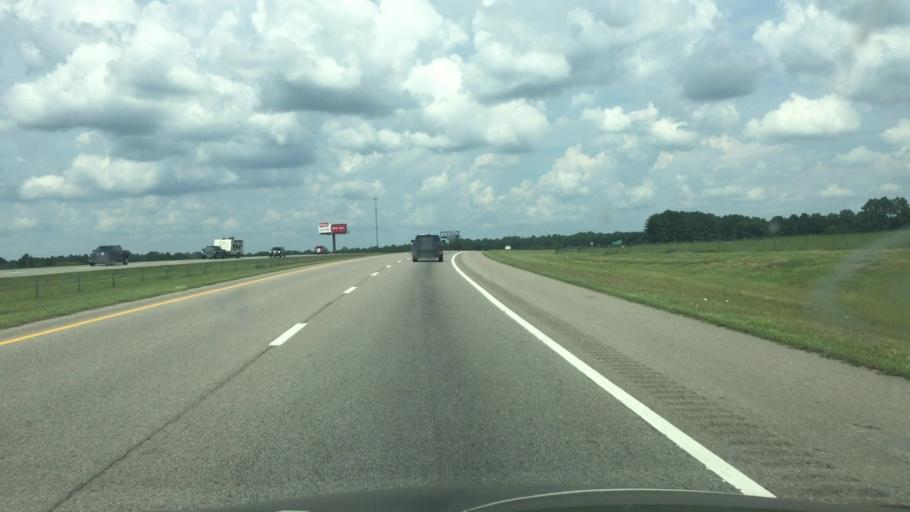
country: US
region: North Carolina
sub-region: Richmond County
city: Ellerbe
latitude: 35.1893
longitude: -79.7241
